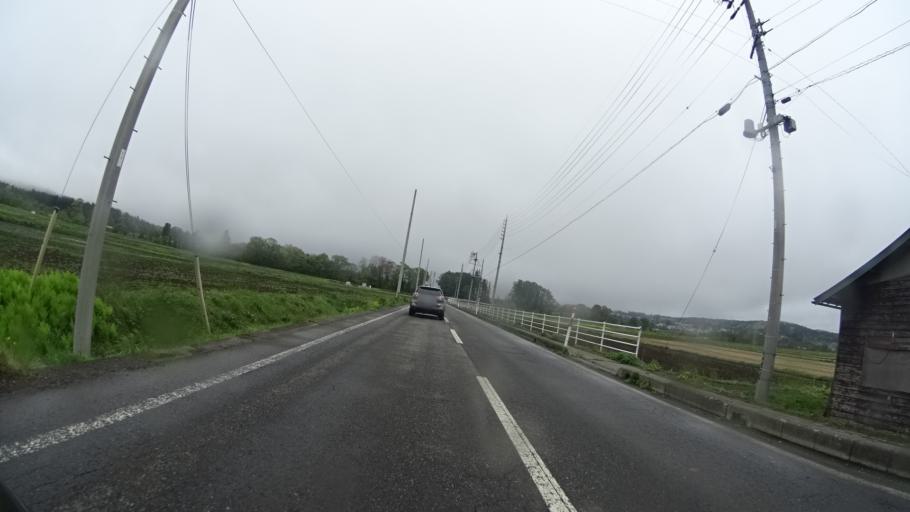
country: JP
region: Nagano
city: Nagano-shi
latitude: 36.7908
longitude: 138.1964
